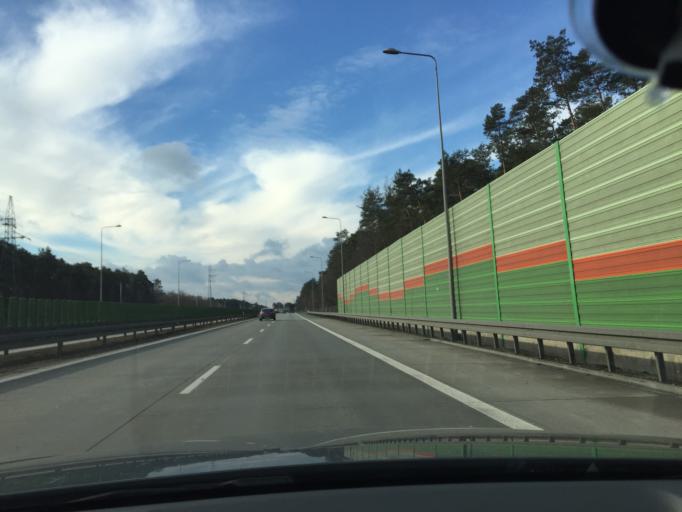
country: PL
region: Lodz Voivodeship
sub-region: Powiat piotrkowski
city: Wolborz
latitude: 51.4565
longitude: 19.7749
